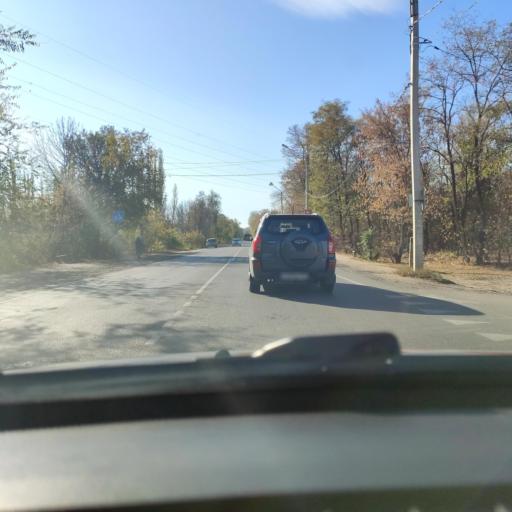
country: RU
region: Voronezj
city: Maslovka
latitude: 51.5942
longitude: 39.1764
